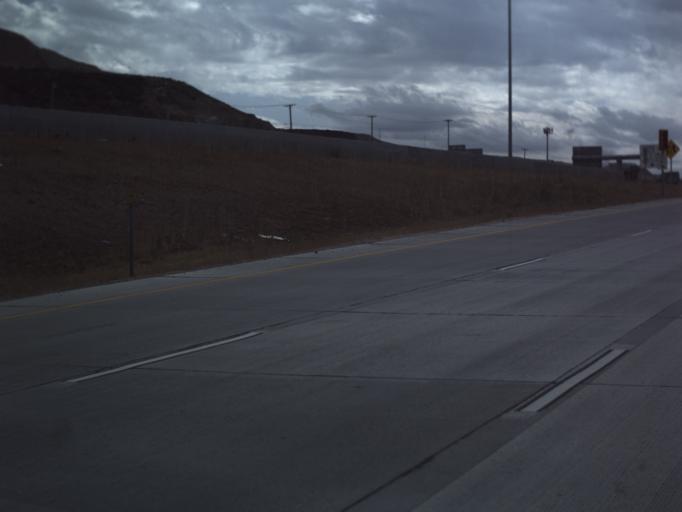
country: US
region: Utah
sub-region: Salt Lake County
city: Bluffdale
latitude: 40.4812
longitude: -111.9024
